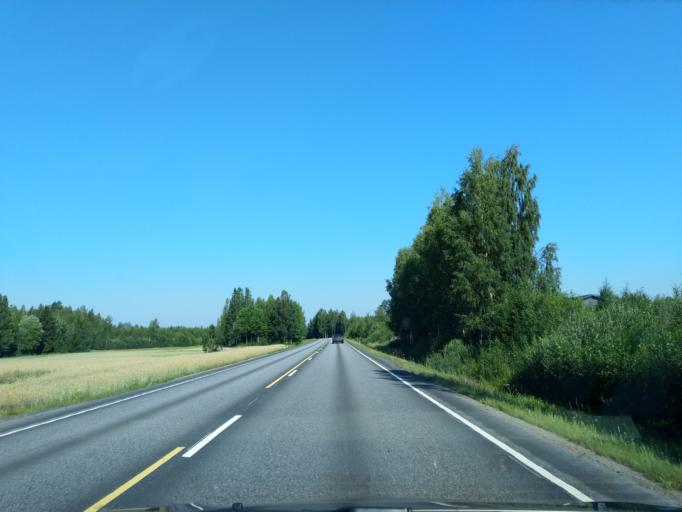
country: FI
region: Satakunta
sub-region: Pori
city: Huittinen
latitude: 61.1605
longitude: 22.7210
